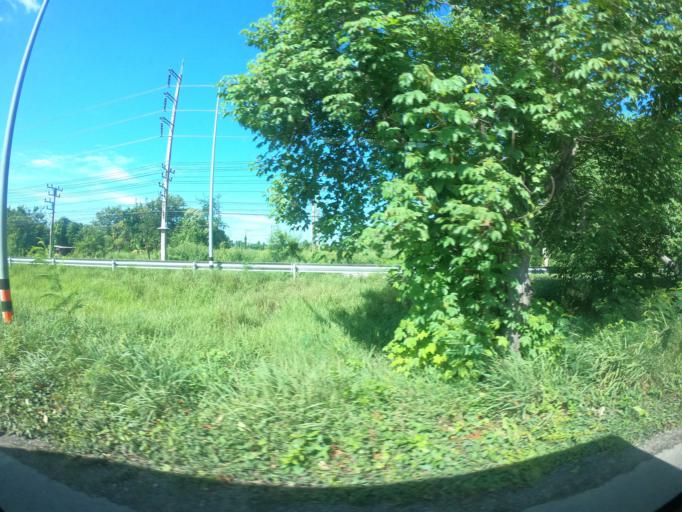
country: TH
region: Nakhon Nayok
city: Nakhon Nayok
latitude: 14.2353
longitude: 101.1602
